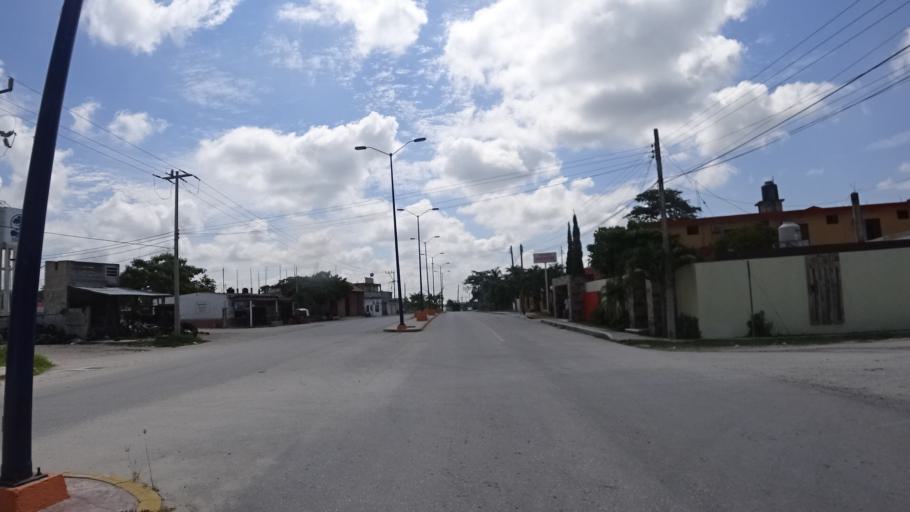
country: MX
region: Campeche
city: Sabancuy
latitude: 18.9692
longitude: -91.1774
